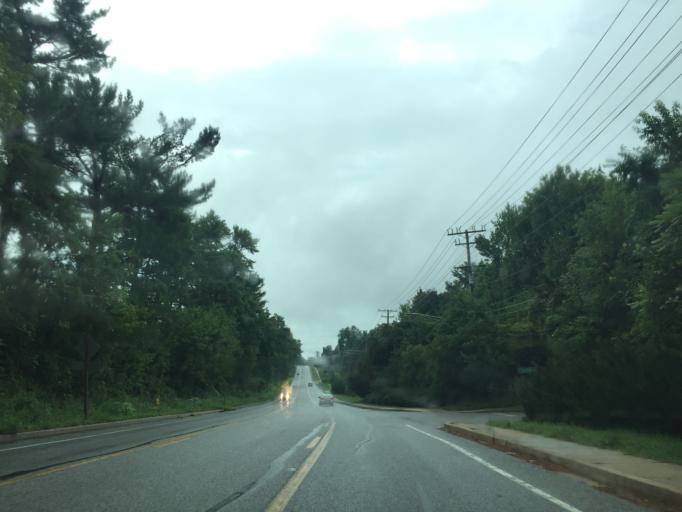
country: US
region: Maryland
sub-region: Harford County
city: South Bel Air
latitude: 39.5207
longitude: -76.3356
